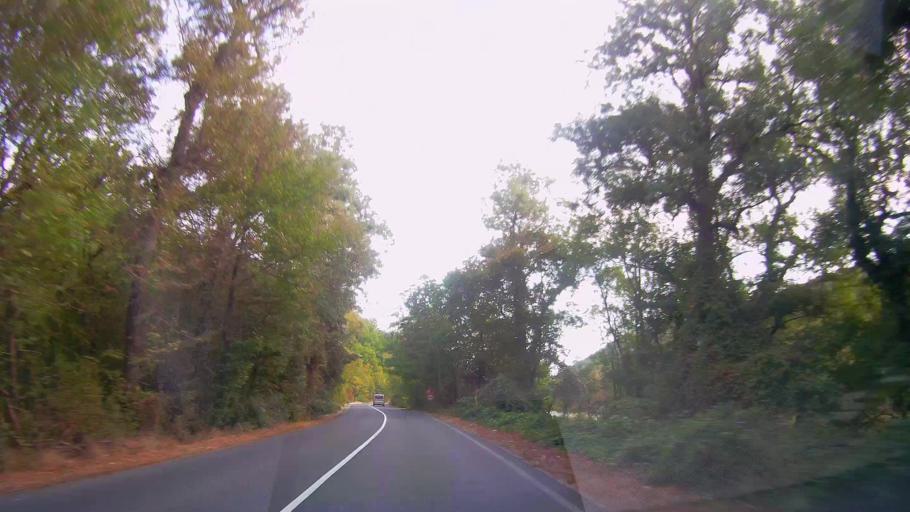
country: BG
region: Burgas
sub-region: Obshtina Primorsko
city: Primorsko
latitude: 42.3108
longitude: 27.7250
